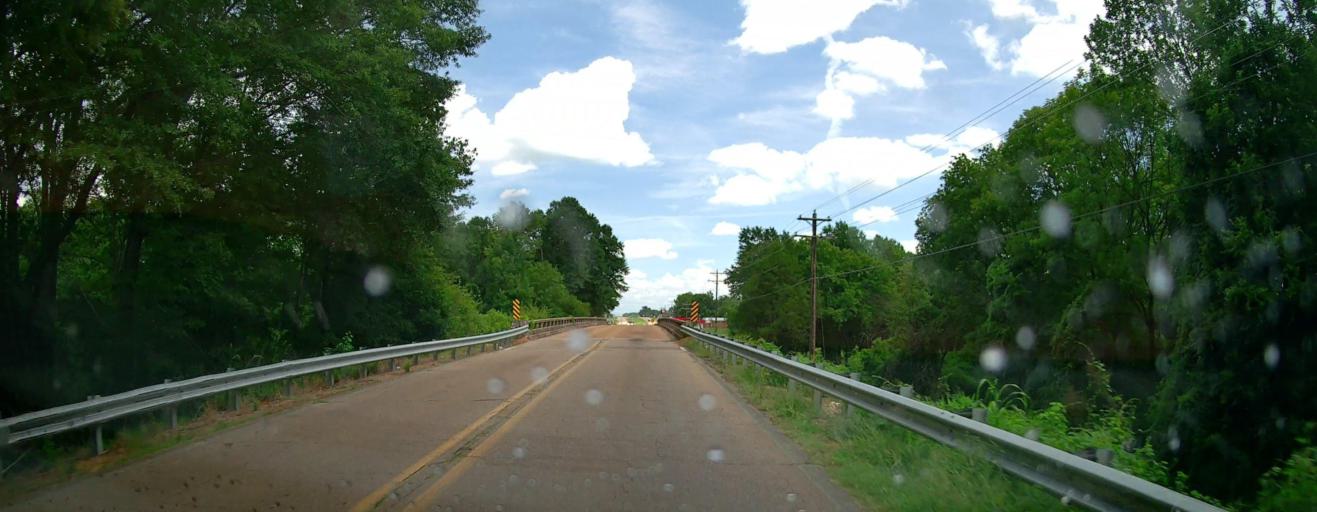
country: US
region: Mississippi
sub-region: Lee County
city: Shannon
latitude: 34.1211
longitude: -88.7119
